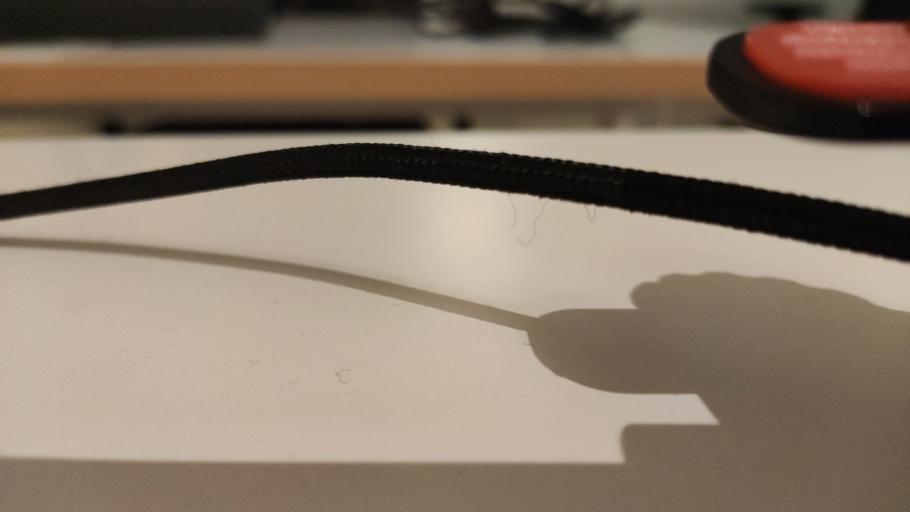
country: RU
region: Moskovskaya
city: Semkhoz
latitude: 56.4066
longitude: 38.0145
